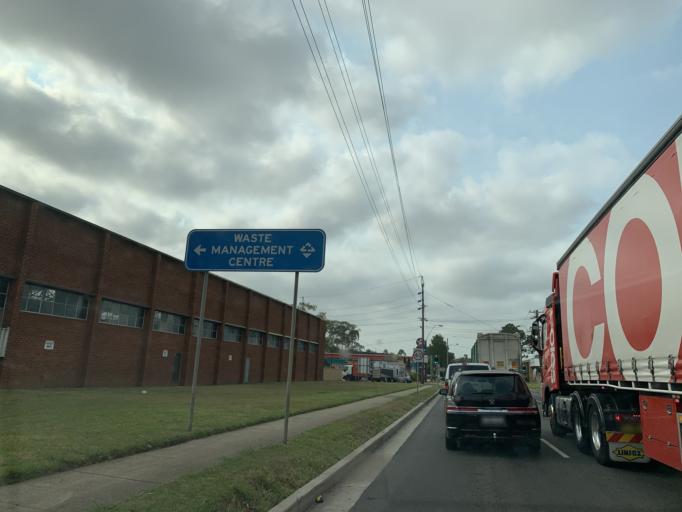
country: AU
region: New South Wales
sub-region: Holroyd
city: Girraween
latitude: -33.7731
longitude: 150.9442
